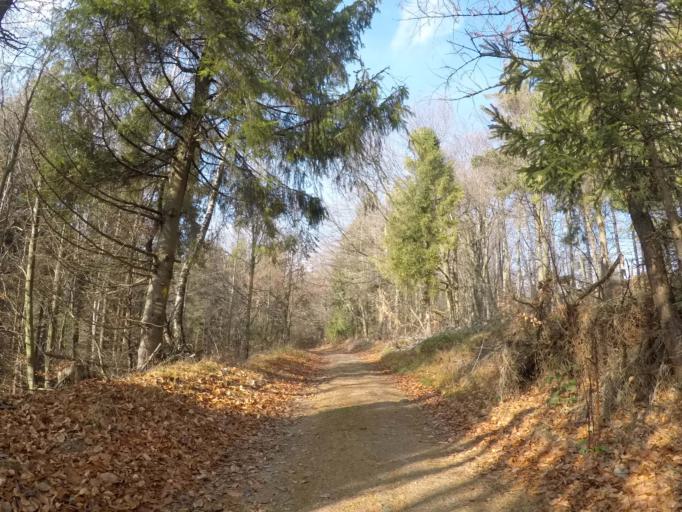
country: SK
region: Kosicky
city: Gelnica
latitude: 48.7630
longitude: 21.0316
